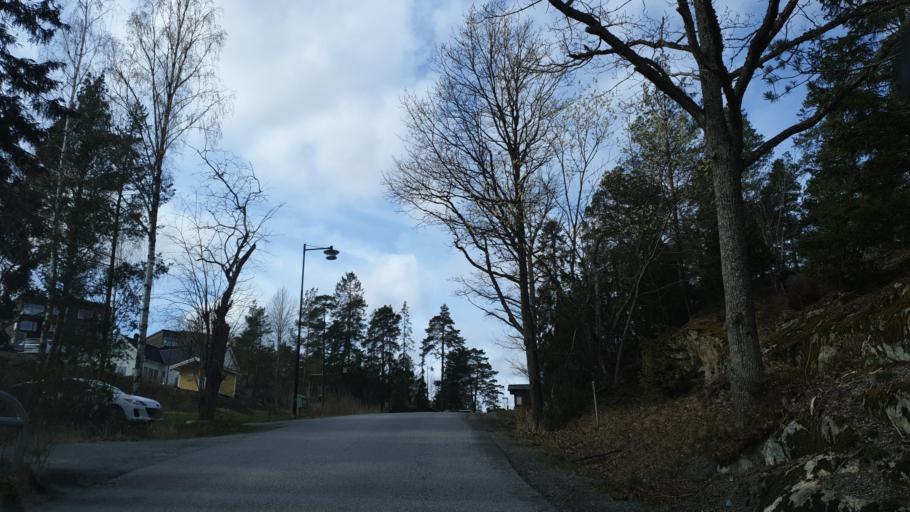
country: SE
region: Stockholm
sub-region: Nacka Kommun
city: Boo
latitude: 59.3314
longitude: 18.2986
